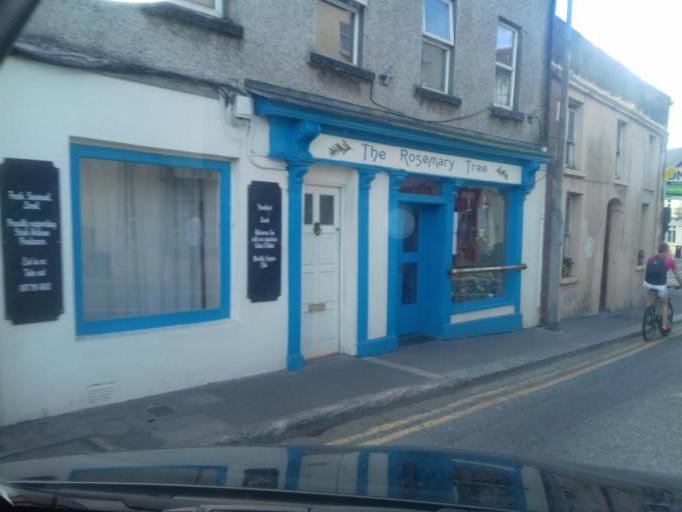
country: IE
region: Leinster
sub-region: Kilkenny
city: Thomastown
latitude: 52.5248
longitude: -7.1383
